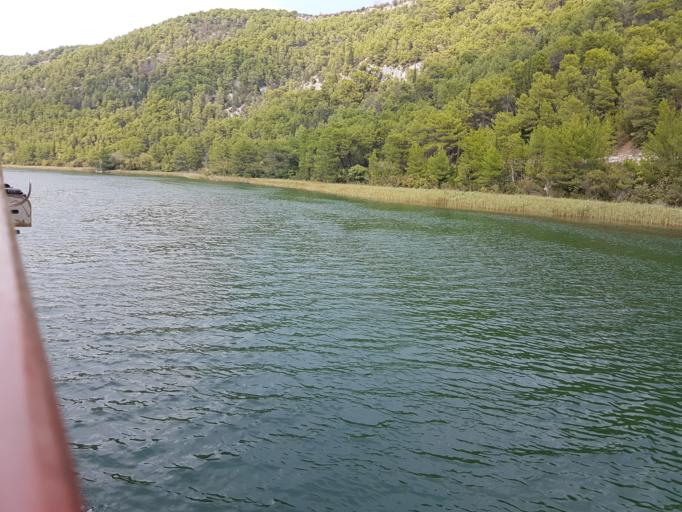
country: HR
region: Sibensko-Kniniska
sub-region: Grad Sibenik
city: Sibenik
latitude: 43.8175
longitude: 15.9497
